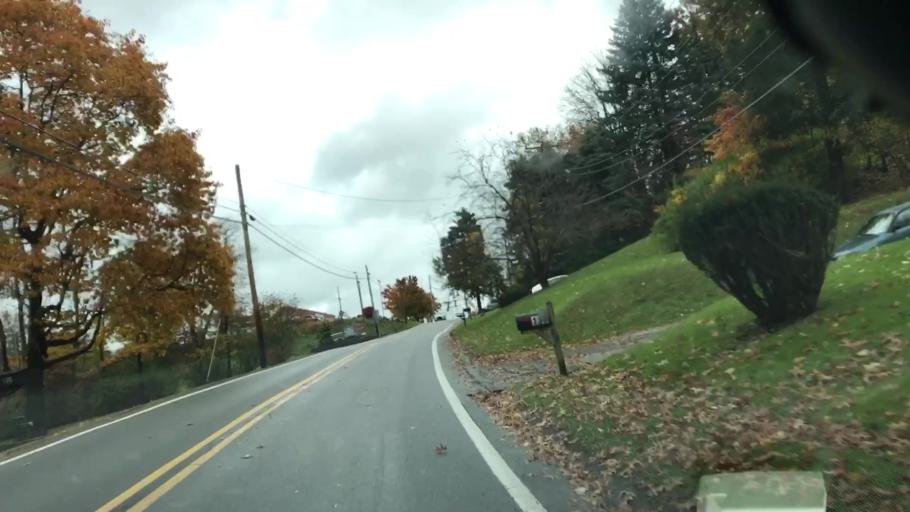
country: US
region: Pennsylvania
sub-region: Allegheny County
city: Bradford Woods
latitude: 40.6092
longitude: -80.0556
